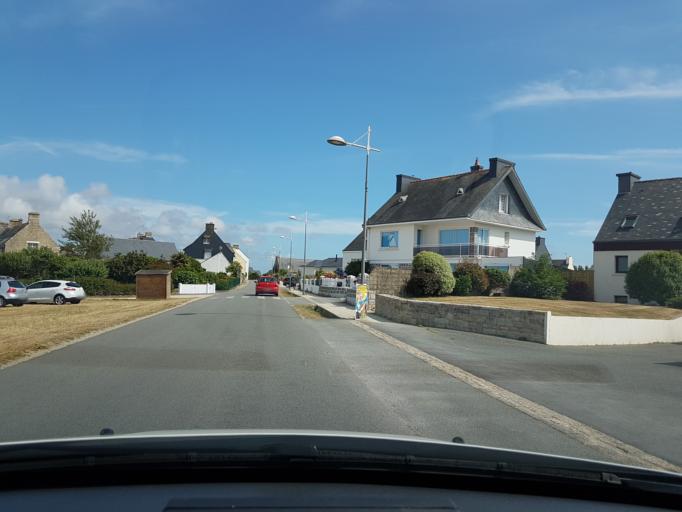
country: FR
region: Brittany
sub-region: Departement du Morbihan
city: Etel
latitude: 47.6634
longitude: -3.2189
